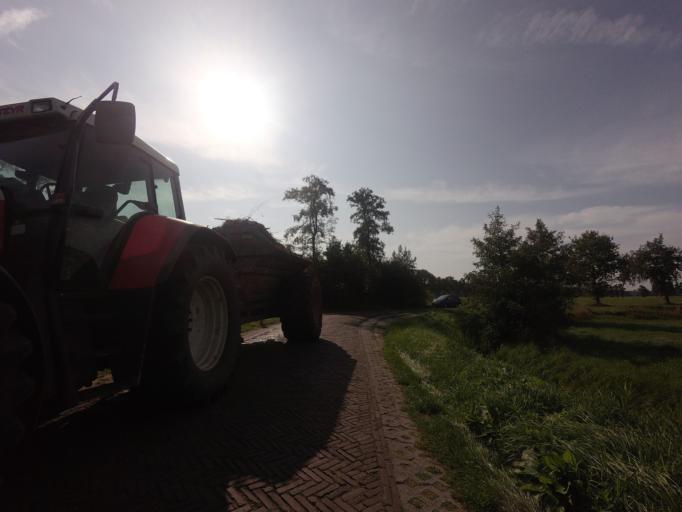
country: NL
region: Groningen
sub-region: Gemeente Leek
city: Leek
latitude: 53.1671
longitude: 6.4130
